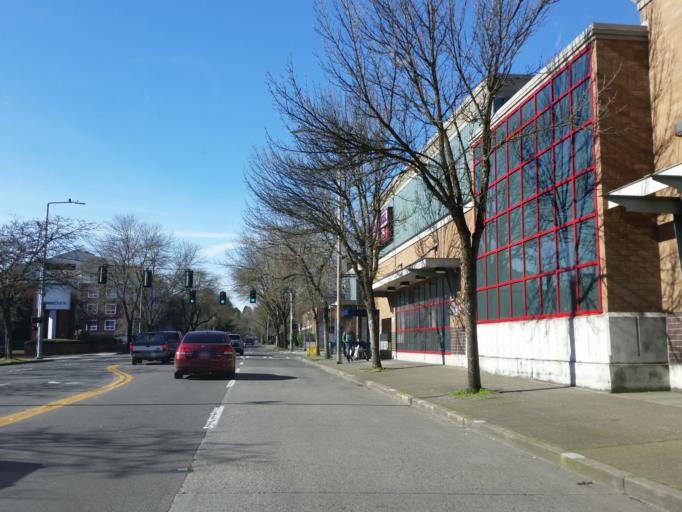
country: US
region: Washington
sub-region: King County
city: Lake Forest Park
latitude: 47.7194
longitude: -122.2954
